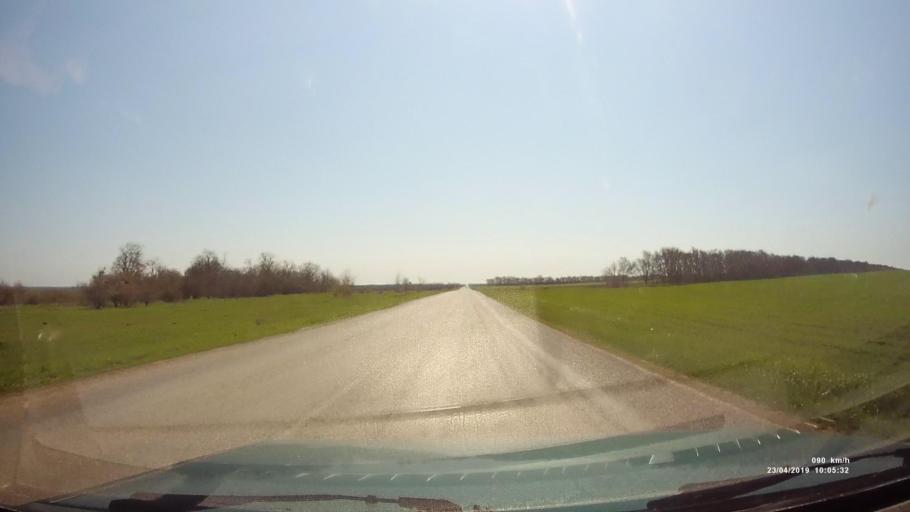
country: RU
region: Rostov
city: Sovetskoye
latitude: 46.7404
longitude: 42.2212
